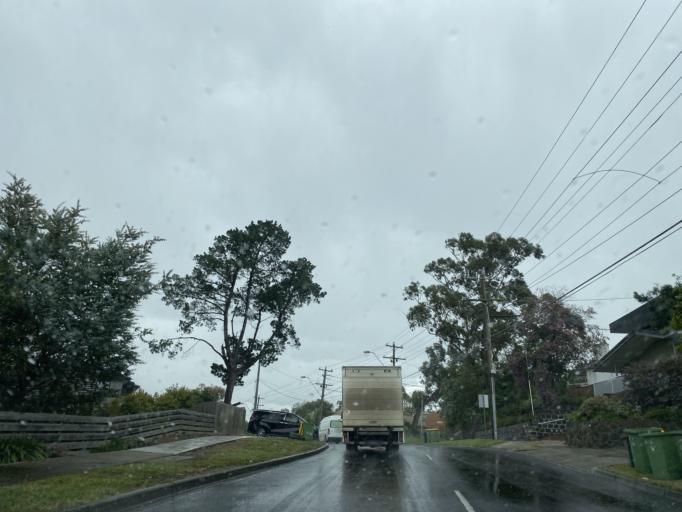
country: AU
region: Victoria
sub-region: Banyule
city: Montmorency
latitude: -37.7243
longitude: 145.1126
